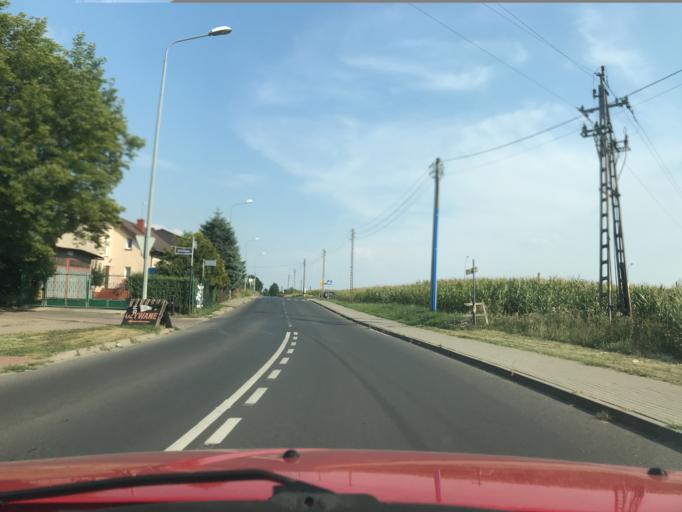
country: PL
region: Greater Poland Voivodeship
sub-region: Powiat poznanski
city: Lubon
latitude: 52.3648
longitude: 16.8586
